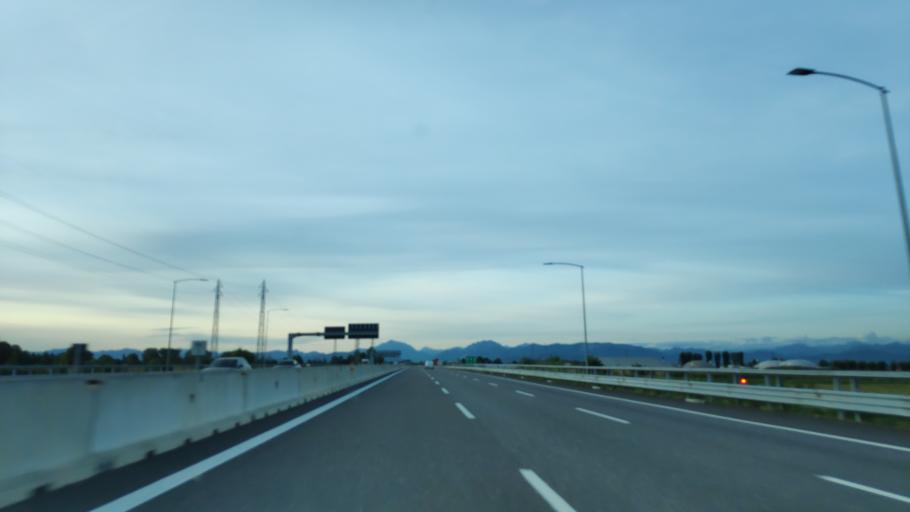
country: IT
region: Lombardy
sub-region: Citta metropolitana di Milano
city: Pozzuolo Martesana
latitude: 45.5211
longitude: 9.4400
